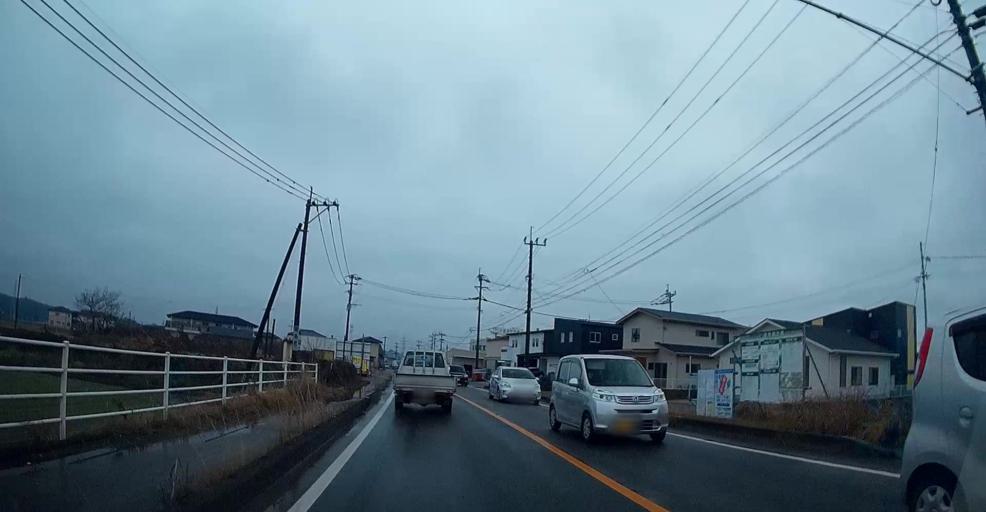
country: JP
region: Kumamoto
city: Uto
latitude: 32.7311
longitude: 130.7380
